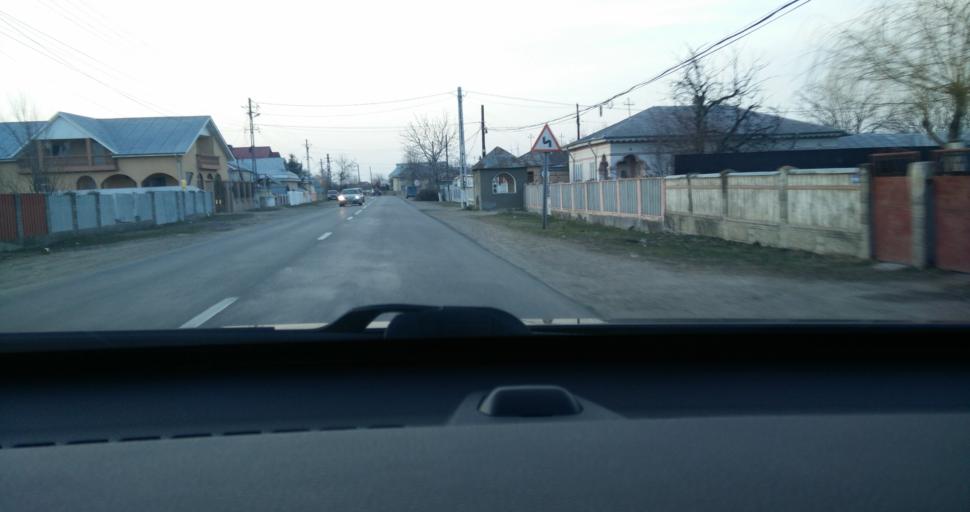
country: RO
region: Vrancea
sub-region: Comuna Rastoaca
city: Rastoaca
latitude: 45.6612
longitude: 27.2811
